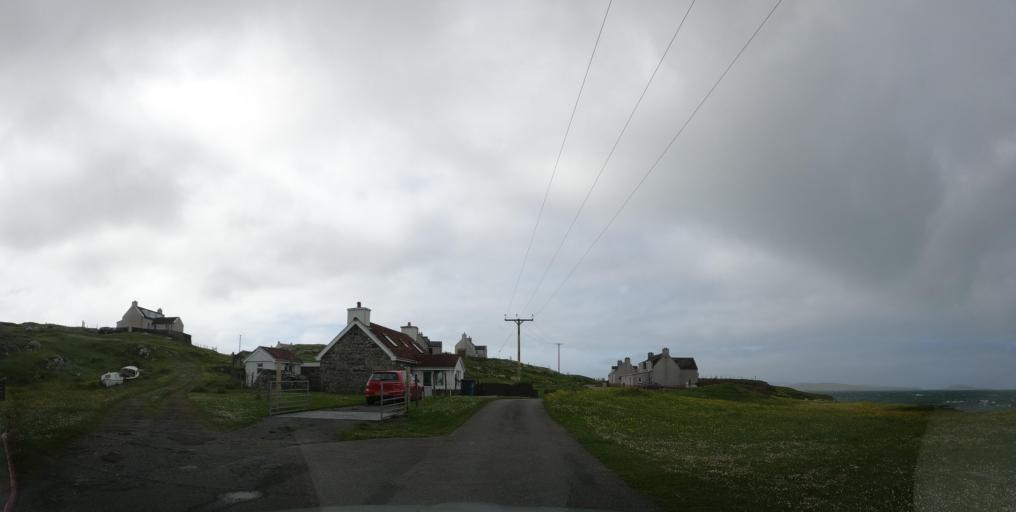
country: GB
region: Scotland
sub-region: Eilean Siar
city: Isle of South Uist
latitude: 57.0831
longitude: -7.3093
